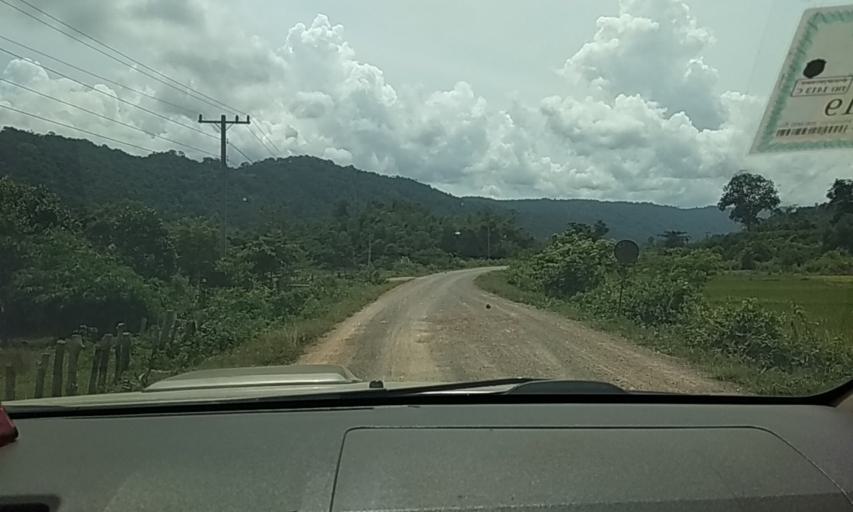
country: LA
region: Bolikhamxai
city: Ban Nahin
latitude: 18.1513
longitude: 104.7311
